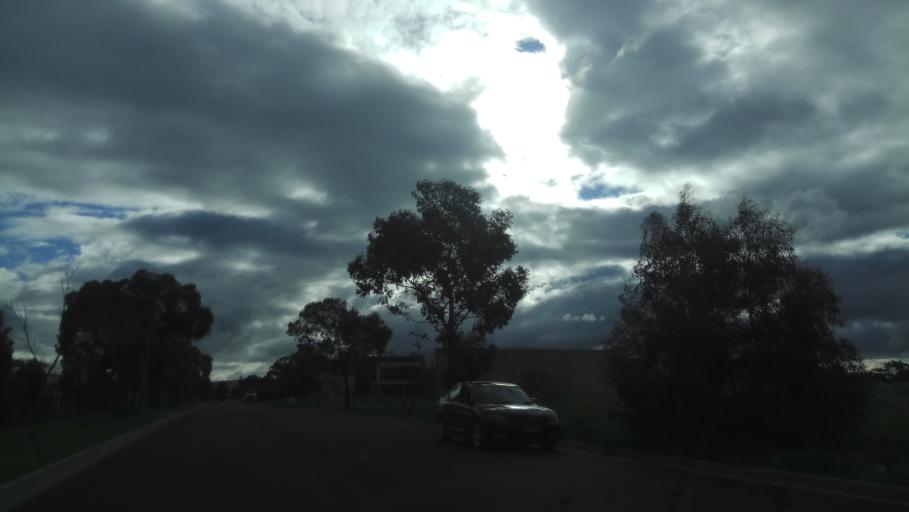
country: AU
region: Victoria
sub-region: Hobsons Bay
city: Altona
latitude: -37.8559
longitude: 144.8140
